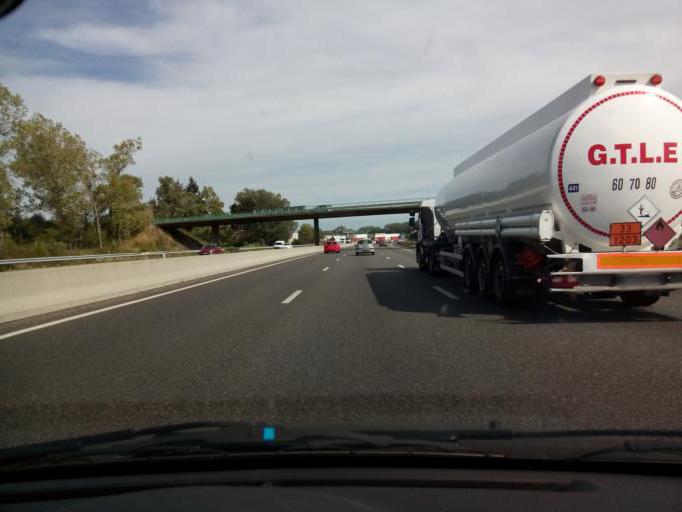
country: FR
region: Rhone-Alpes
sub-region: Departement de l'Isere
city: La Verpilliere
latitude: 45.6458
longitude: 5.1332
